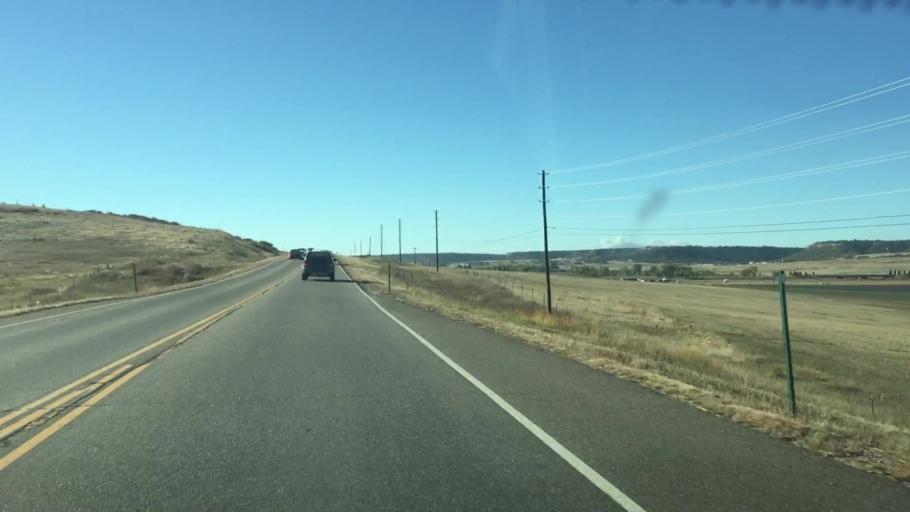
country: US
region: Colorado
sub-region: Douglas County
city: The Pinery
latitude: 39.4261
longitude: -104.7607
